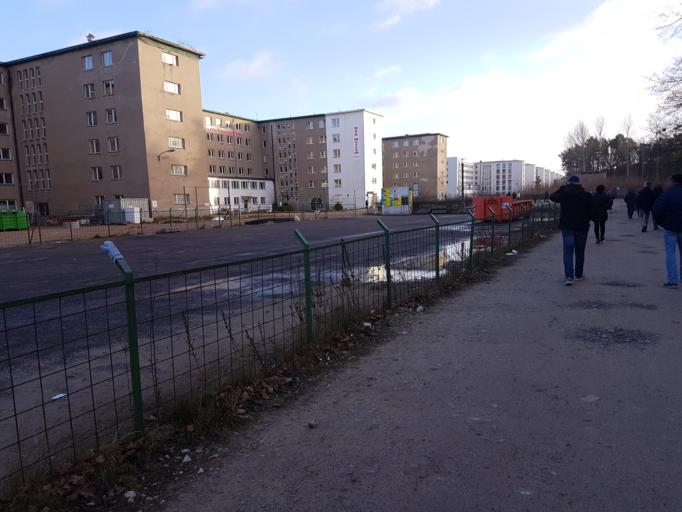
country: DE
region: Mecklenburg-Vorpommern
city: Ostseebad Binz
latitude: 54.4364
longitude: 13.5760
